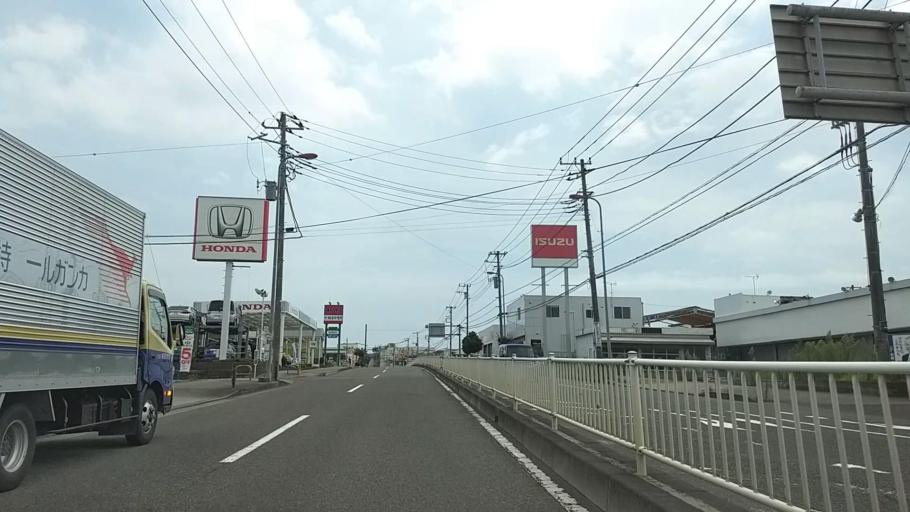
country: JP
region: Kanagawa
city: Minami-rinkan
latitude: 35.4546
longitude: 139.4174
